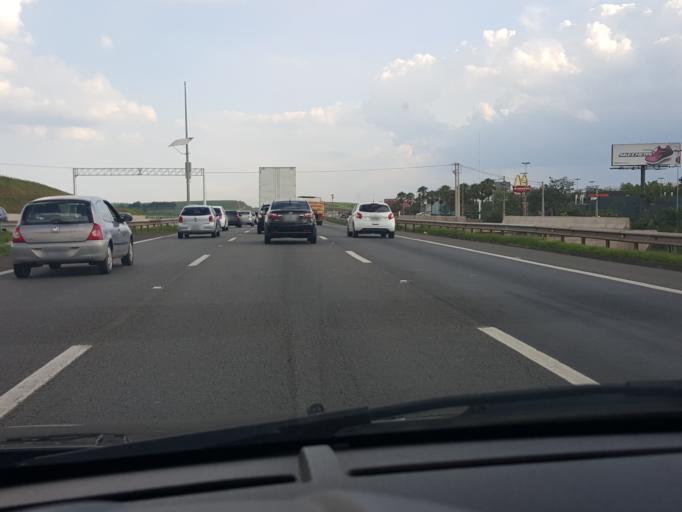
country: BR
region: Sao Paulo
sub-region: Campinas
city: Campinas
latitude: -22.8606
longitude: -47.0227
